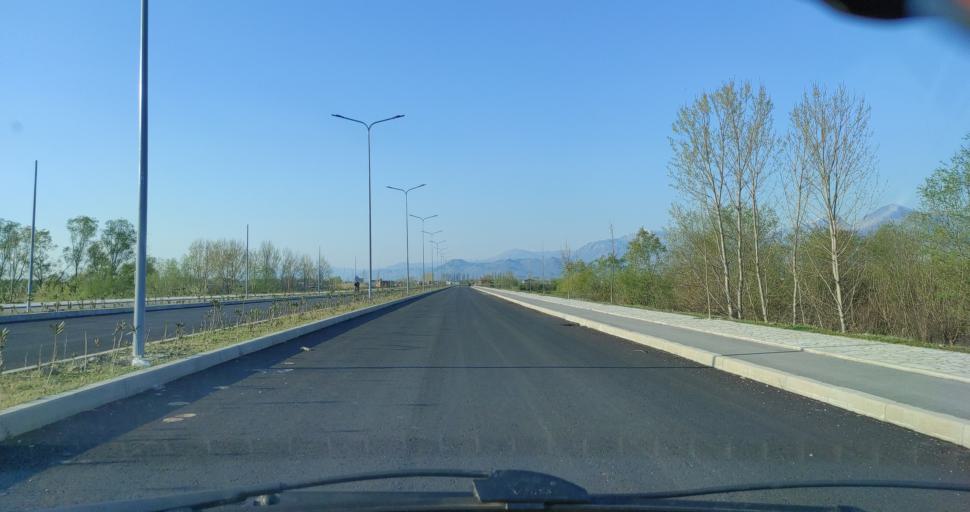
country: AL
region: Shkoder
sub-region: Rrethi i Shkodres
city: Shkoder
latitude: 42.0686
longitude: 19.4894
